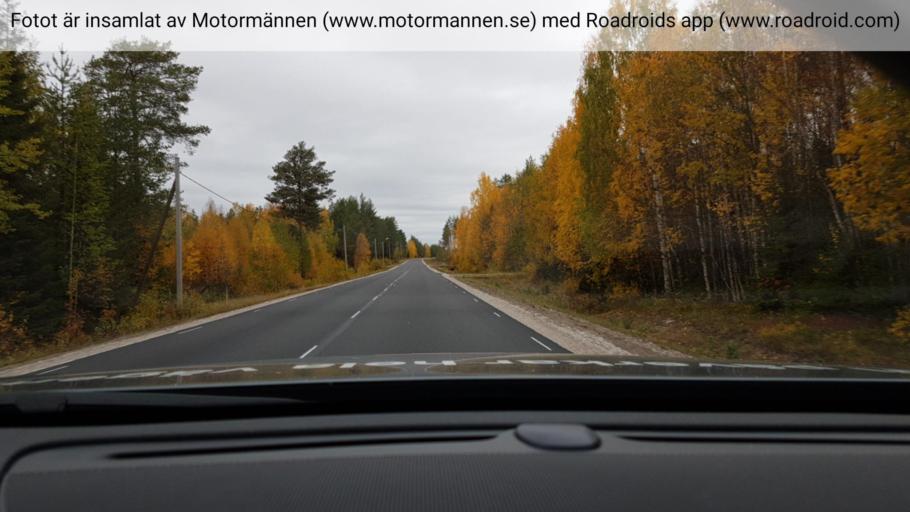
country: SE
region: Norrbotten
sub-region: Overkalix Kommun
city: OEverkalix
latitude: 66.3860
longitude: 22.8256
